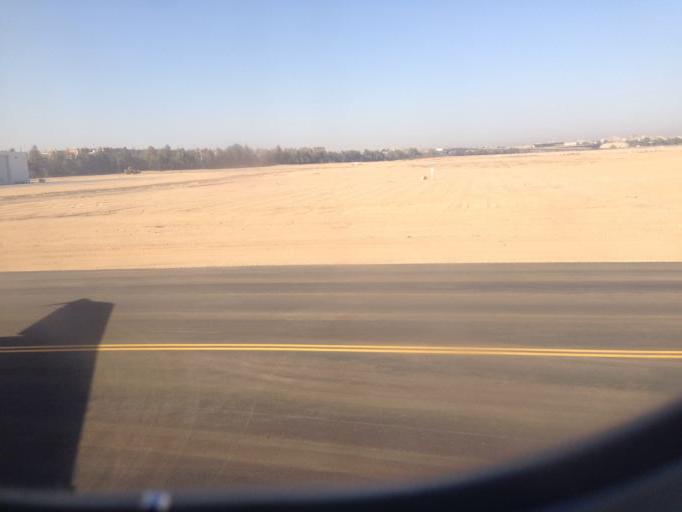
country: EG
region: Muhafazat al Qalyubiyah
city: Al Khankah
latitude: 30.1188
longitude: 31.3814
